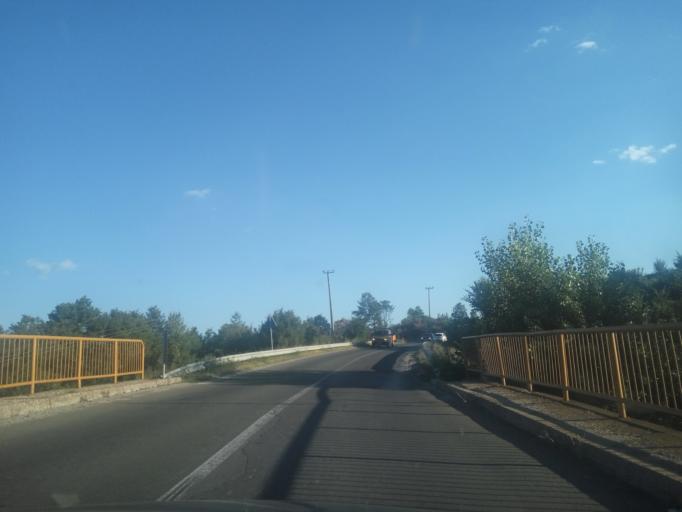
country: XK
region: Gjakova
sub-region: Komuna e Gjakoves
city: Gjakove
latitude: 42.4579
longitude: 20.5075
